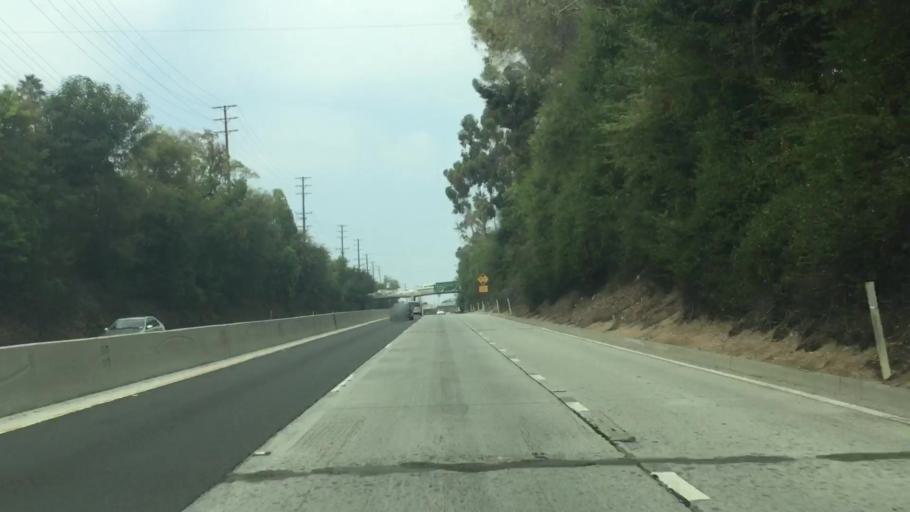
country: US
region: California
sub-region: Los Angeles County
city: South Pasadena
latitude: 34.1191
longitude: -118.1548
